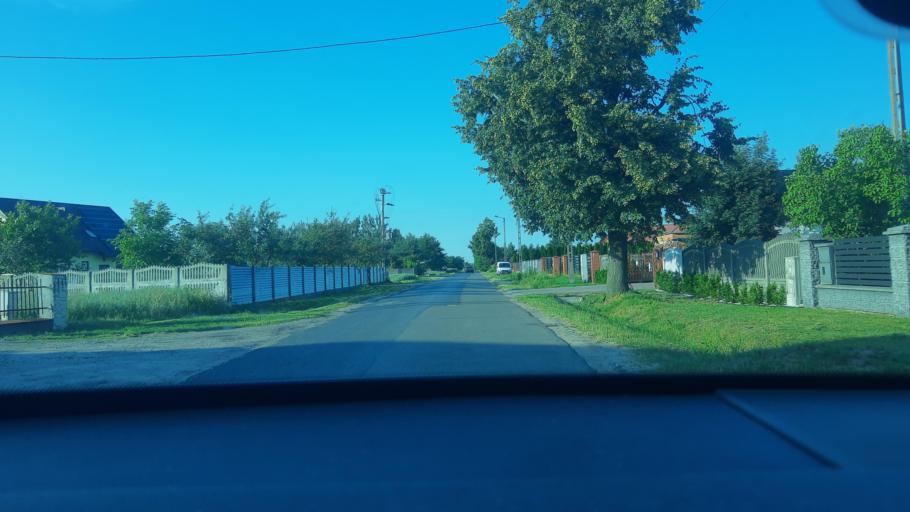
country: PL
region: Lodz Voivodeship
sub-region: Powiat sieradzki
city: Sieradz
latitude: 51.5491
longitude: 18.7574
